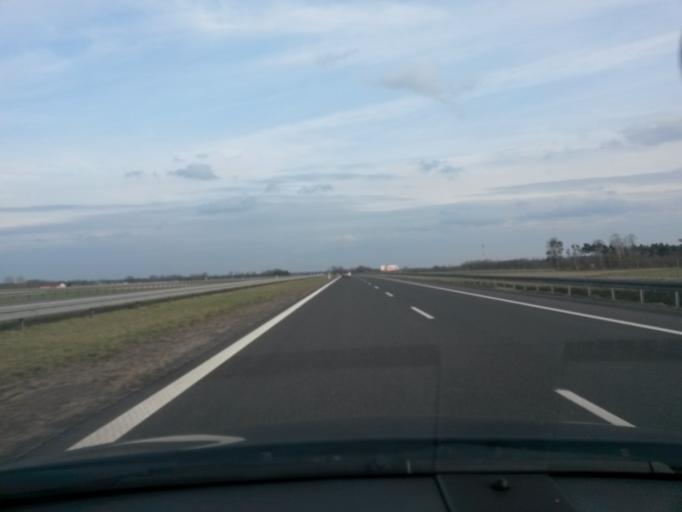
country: PL
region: Lodz Voivodeship
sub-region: Powiat poddebicki
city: Wartkowice
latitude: 51.9811
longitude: 19.0711
